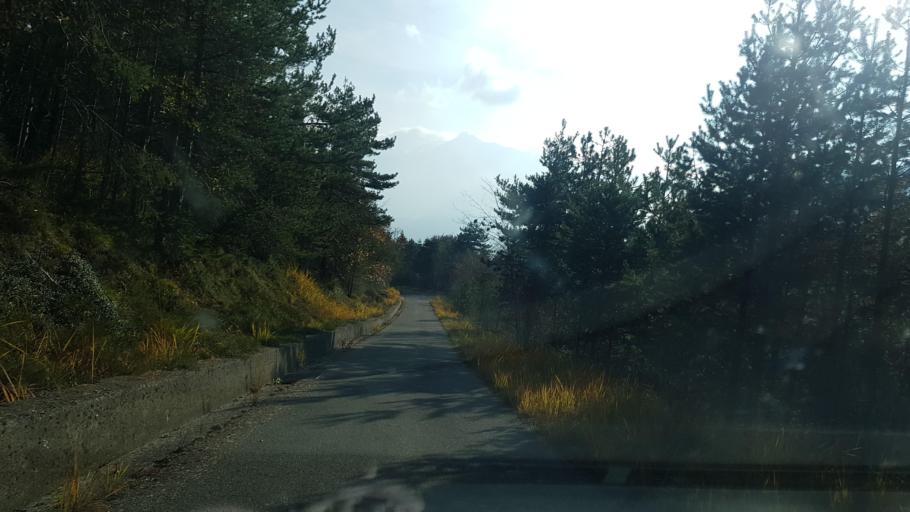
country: IT
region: Friuli Venezia Giulia
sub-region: Provincia di Udine
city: Moggio Udinese
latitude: 46.4437
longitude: 13.2037
